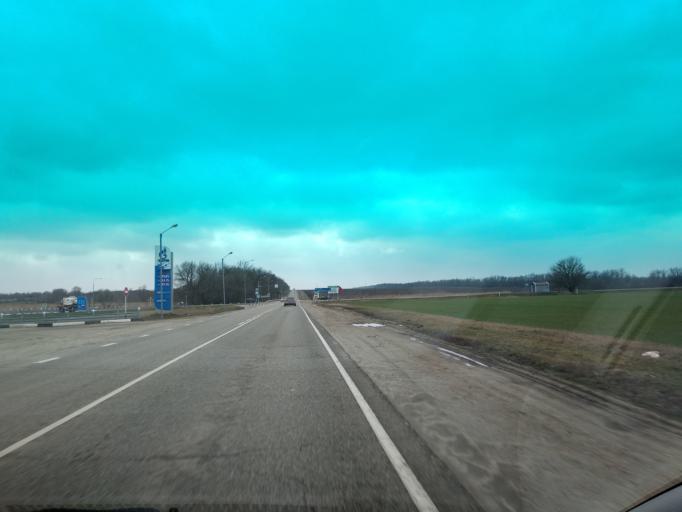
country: RU
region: Krasnodarskiy
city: Novorozhdestvenskaya
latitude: 45.7554
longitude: 39.9241
